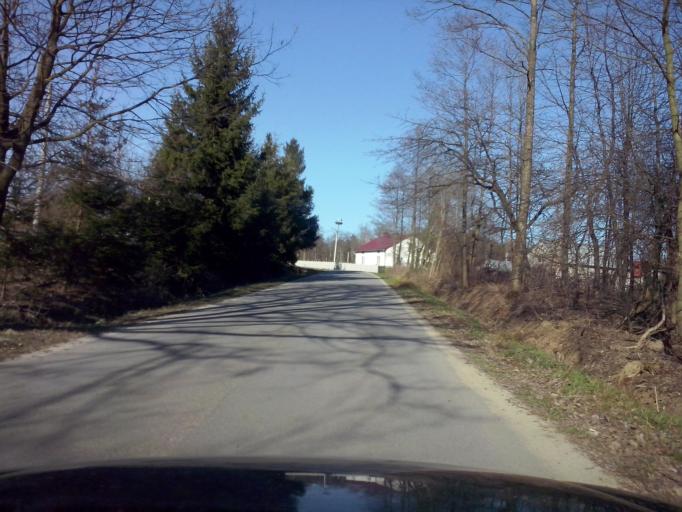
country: PL
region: Subcarpathian Voivodeship
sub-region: Powiat nizanski
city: Krzeszow
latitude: 50.3936
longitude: 22.4009
